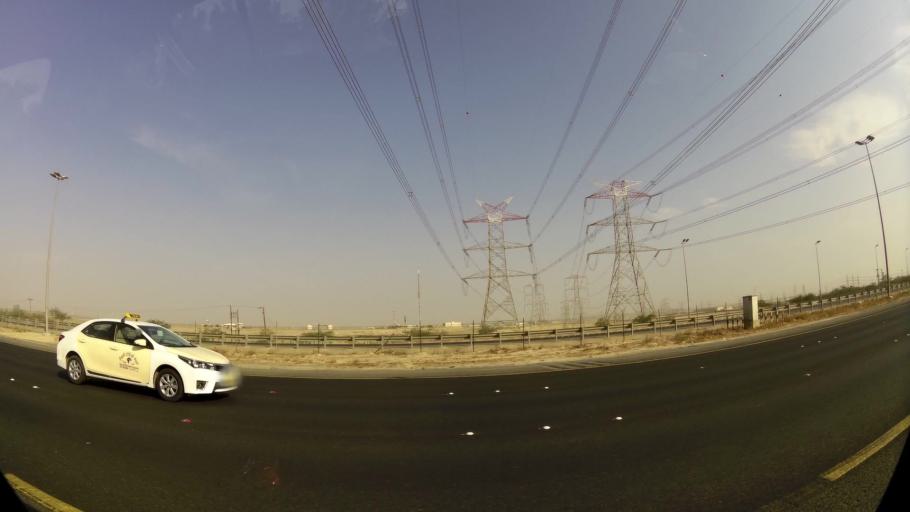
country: KW
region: Mubarak al Kabir
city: Mubarak al Kabir
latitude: 29.1725
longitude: 48.0498
